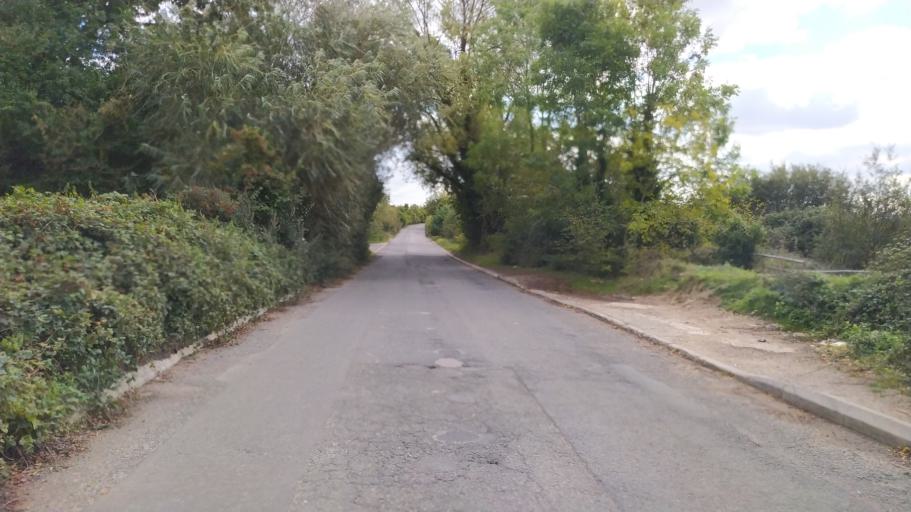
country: GB
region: England
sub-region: Reading
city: Reading
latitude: 51.4228
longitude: -0.9976
